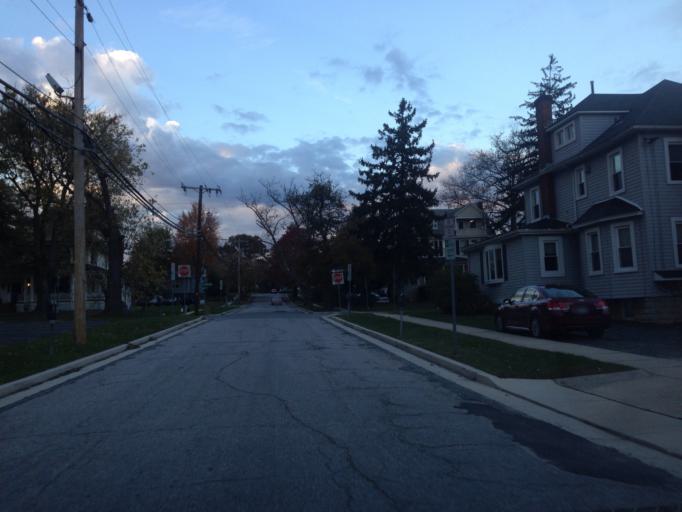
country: US
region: Maryland
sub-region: Baltimore County
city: Towson
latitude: 39.4007
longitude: -76.6099
